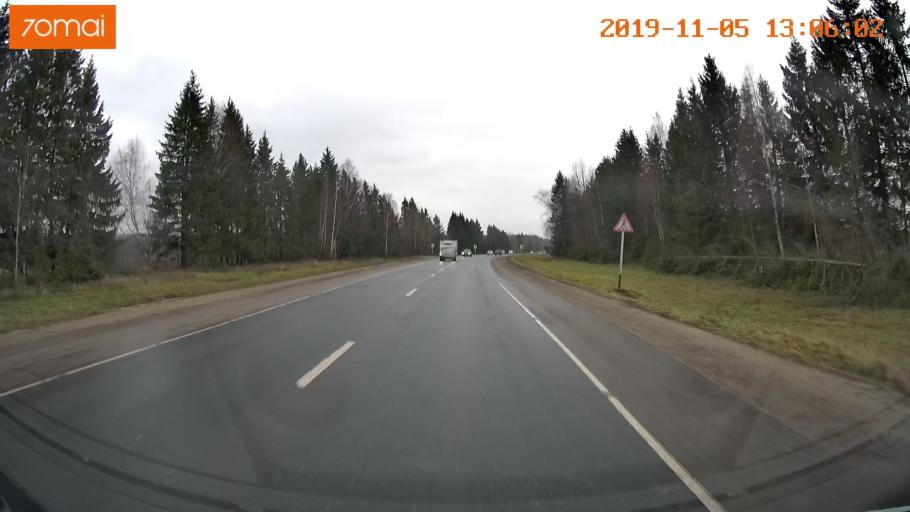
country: RU
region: Ivanovo
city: Kitovo
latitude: 56.8788
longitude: 41.2554
